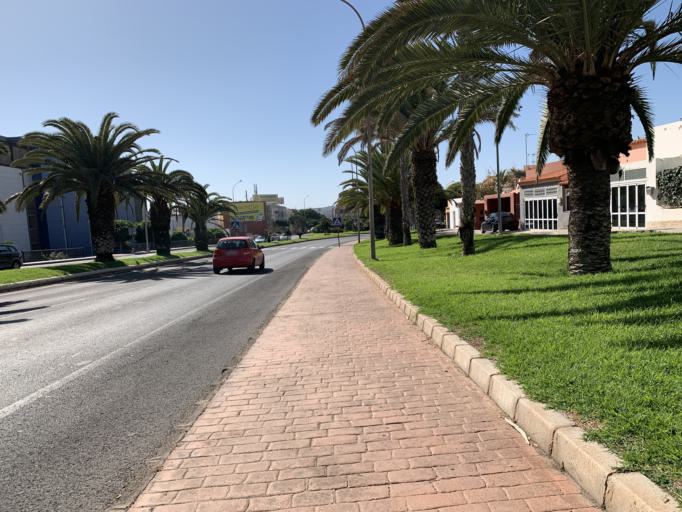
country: ES
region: Canary Islands
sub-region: Provincia de Las Palmas
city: Puerto del Rosario
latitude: 28.4965
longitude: -13.8642
